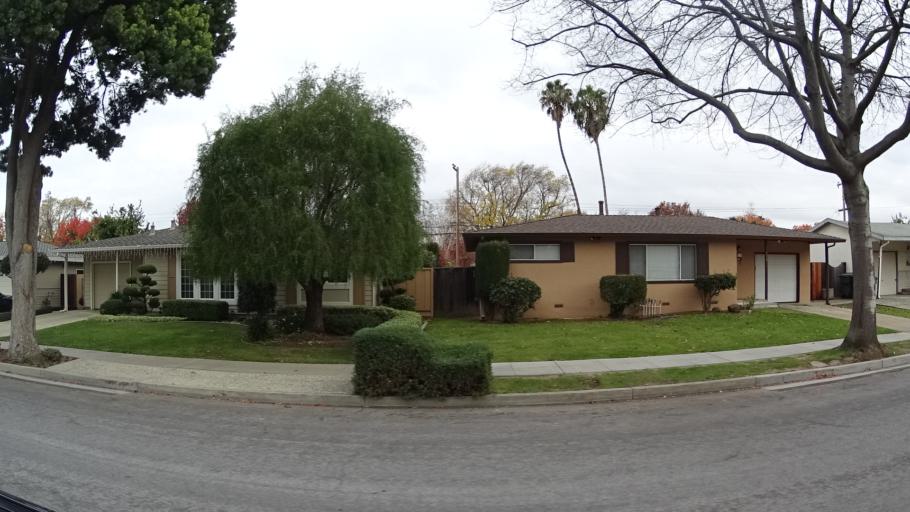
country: US
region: California
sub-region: Santa Clara County
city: Sunnyvale
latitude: 37.3660
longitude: -122.0531
